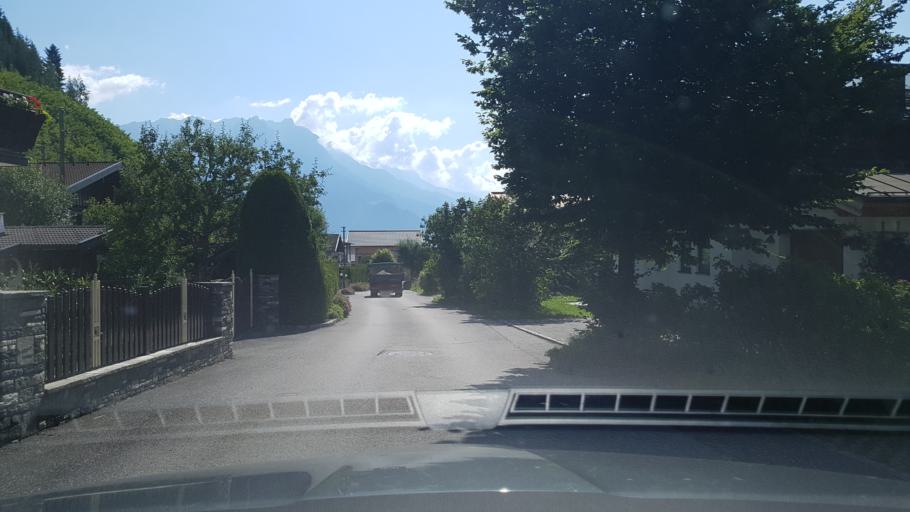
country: AT
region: Salzburg
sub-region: Politischer Bezirk Zell am See
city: Leogang
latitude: 47.4452
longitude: 12.7754
